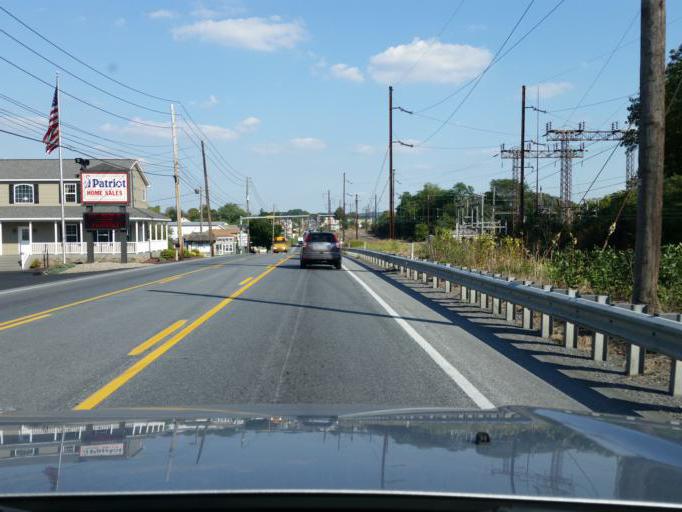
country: US
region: Pennsylvania
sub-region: Lancaster County
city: Intercourse
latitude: 39.9996
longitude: -76.0710
